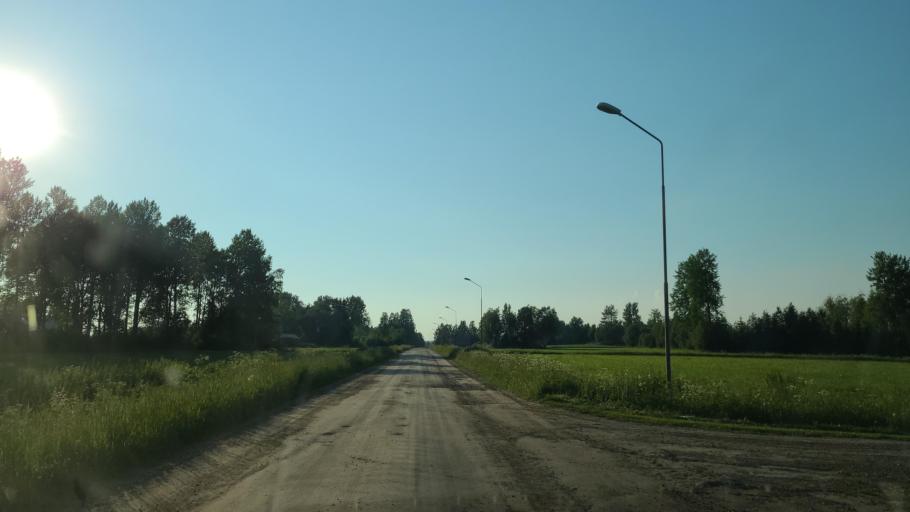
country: SE
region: Vaesterbotten
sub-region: Skelleftea Kommun
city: Burea
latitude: 64.3987
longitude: 21.3754
